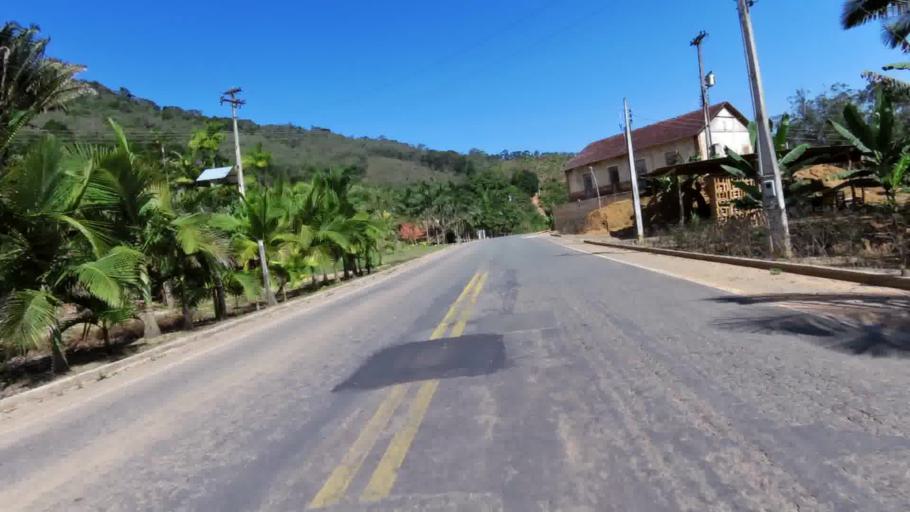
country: BR
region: Espirito Santo
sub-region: Alfredo Chaves
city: Alfredo Chaves
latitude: -20.5430
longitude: -40.7868
